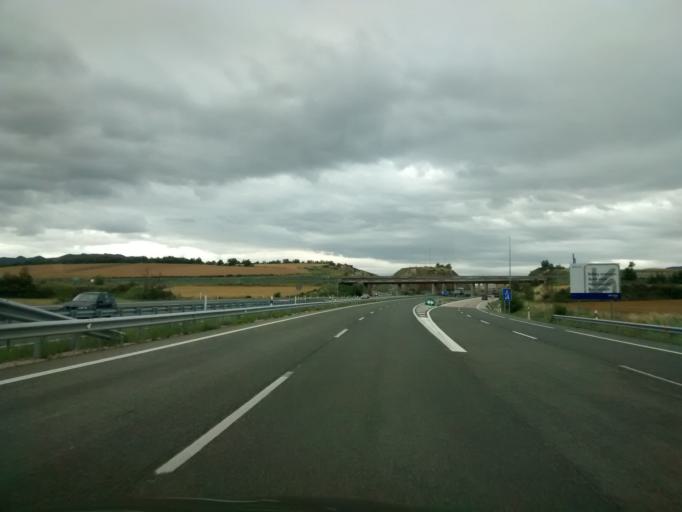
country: ES
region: Basque Country
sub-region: Provincia de Alava
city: Arminon
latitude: 42.7130
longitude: -2.9048
